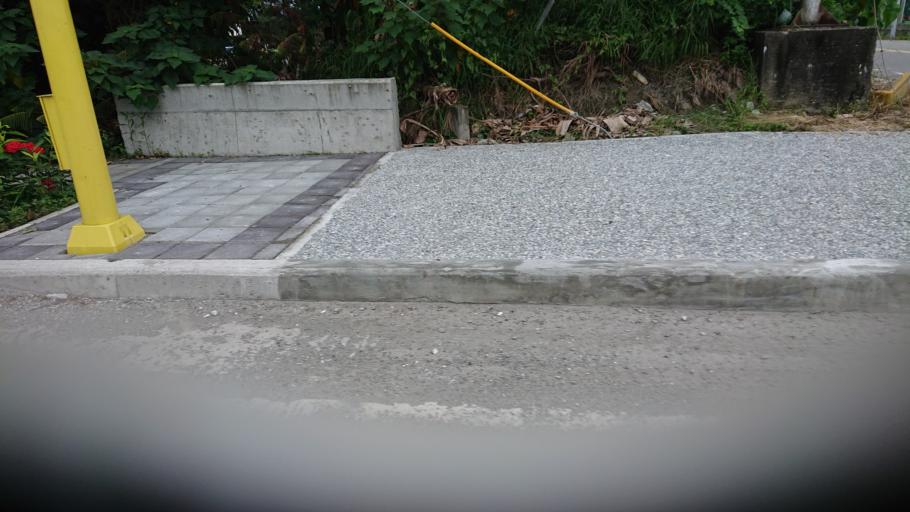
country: TW
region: Taiwan
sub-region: Hualien
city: Hualian
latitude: 23.9598
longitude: 121.6036
